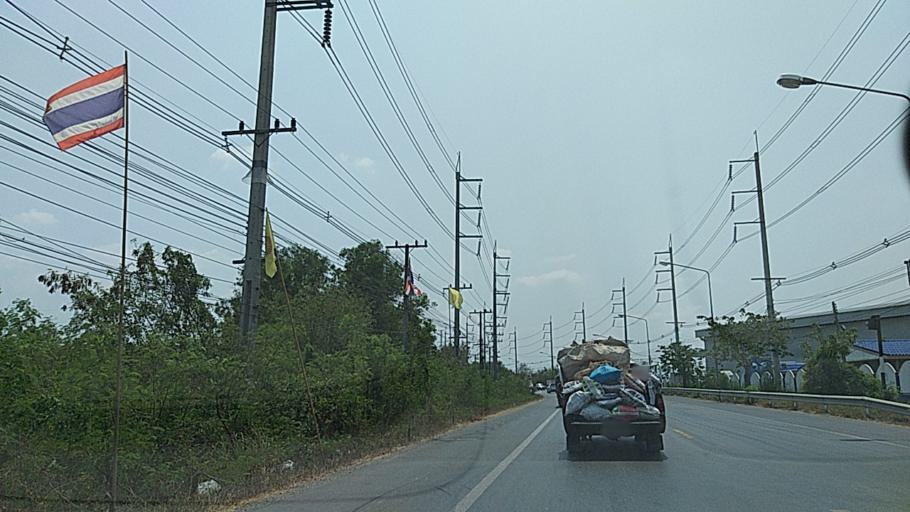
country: TH
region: Chachoengsao
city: Bang Nam Priao
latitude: 13.7943
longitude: 101.0527
